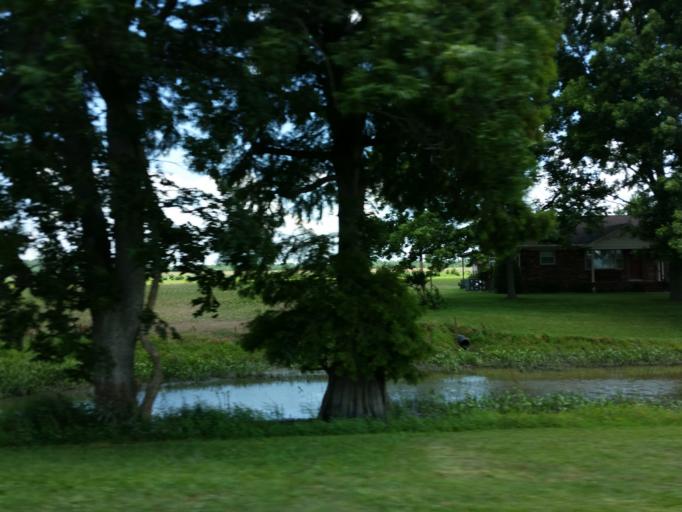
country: US
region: Kentucky
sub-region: Fulton County
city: Hickman
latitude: 36.5494
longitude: -89.2677
